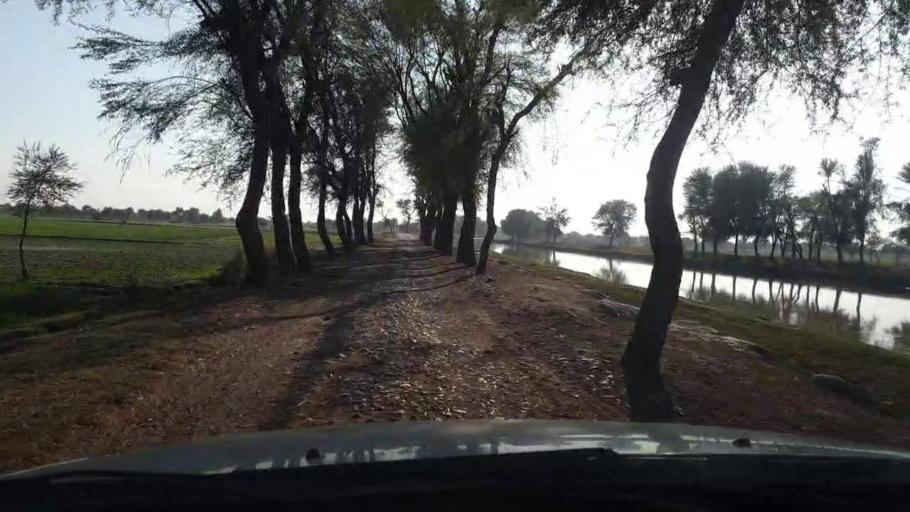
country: PK
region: Sindh
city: Mirpur Mathelo
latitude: 27.9683
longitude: 69.5230
